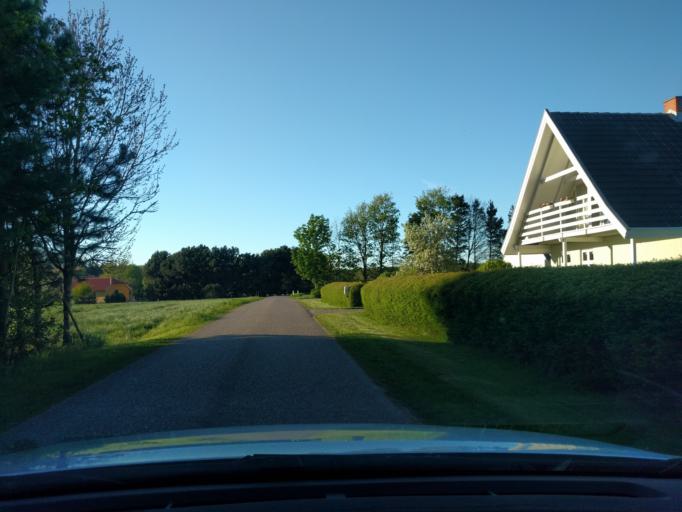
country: DK
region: South Denmark
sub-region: Nyborg Kommune
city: Ullerslev
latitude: 55.3980
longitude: 10.6481
